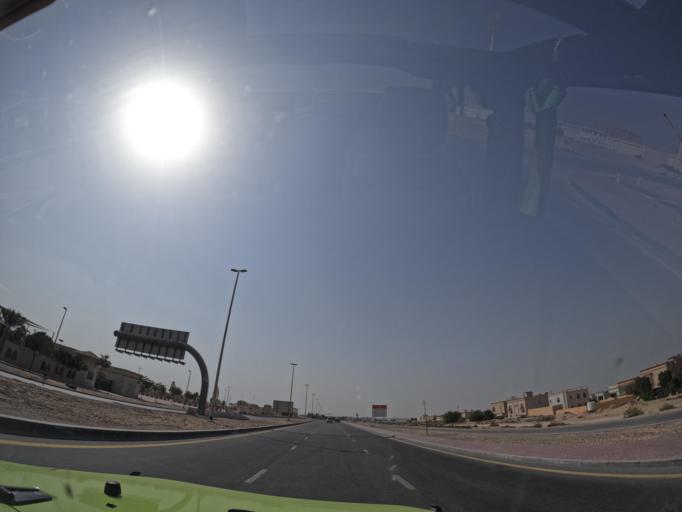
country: AE
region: Ash Shariqah
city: Sharjah
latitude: 25.2015
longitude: 55.4378
